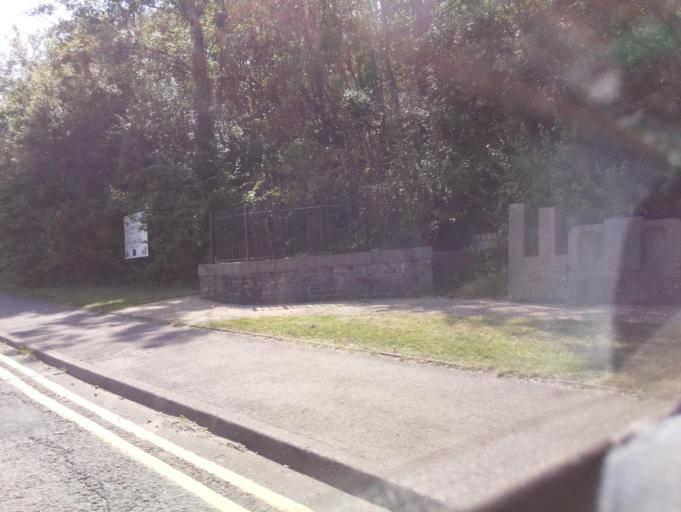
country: GB
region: Wales
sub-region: Caerphilly County Borough
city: Llanbradach
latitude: 51.6100
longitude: -3.2273
